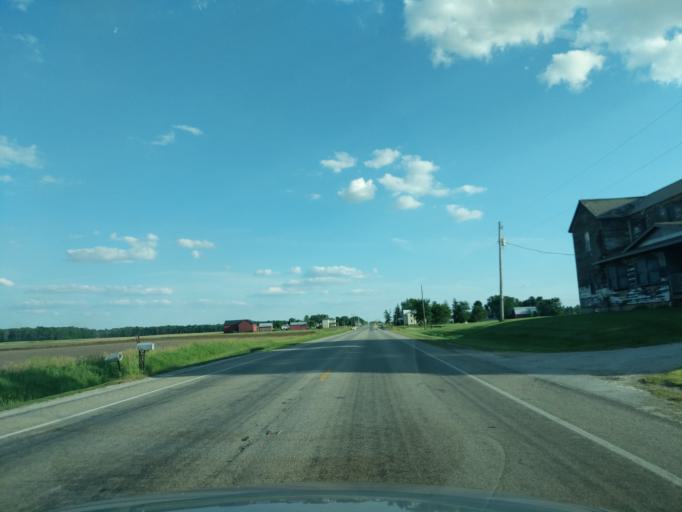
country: US
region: Indiana
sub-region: Whitley County
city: Columbia City
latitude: 41.0578
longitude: -85.4705
